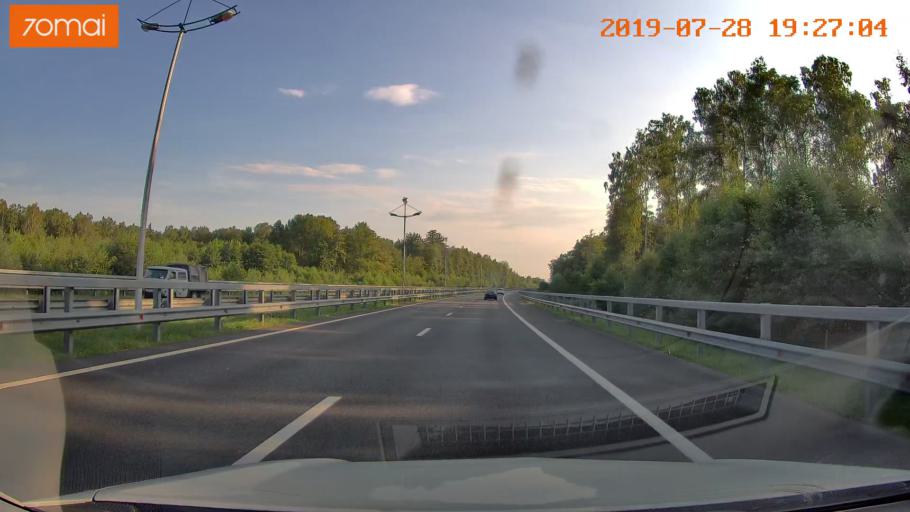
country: RU
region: Kaliningrad
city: Gur'yevsk
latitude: 54.8225
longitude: 20.5748
